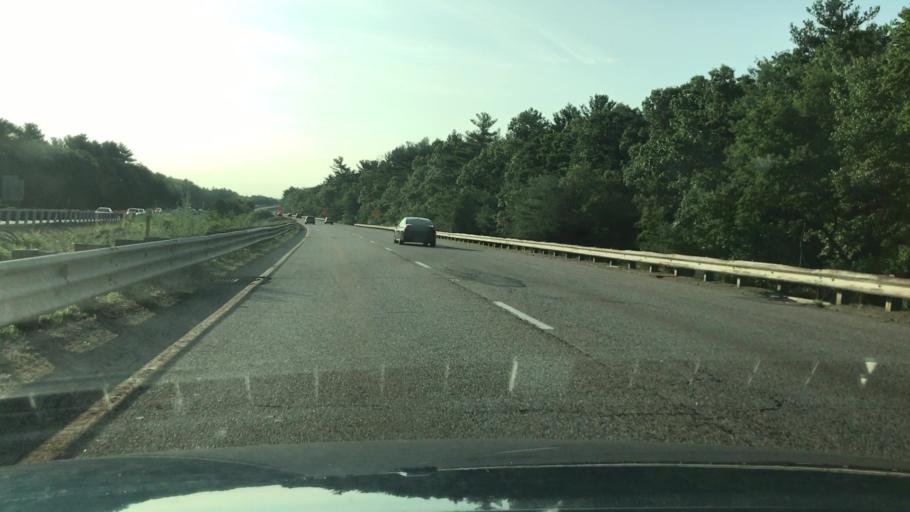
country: US
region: Massachusetts
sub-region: Plymouth County
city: Rockland
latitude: 42.1584
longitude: -70.8724
